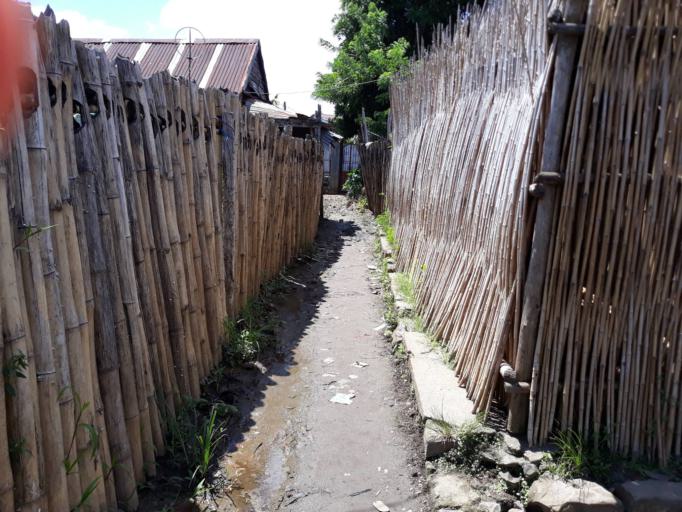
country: MG
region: Atsinanana
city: Ampasimanolotra
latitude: -18.8200
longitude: 49.0728
